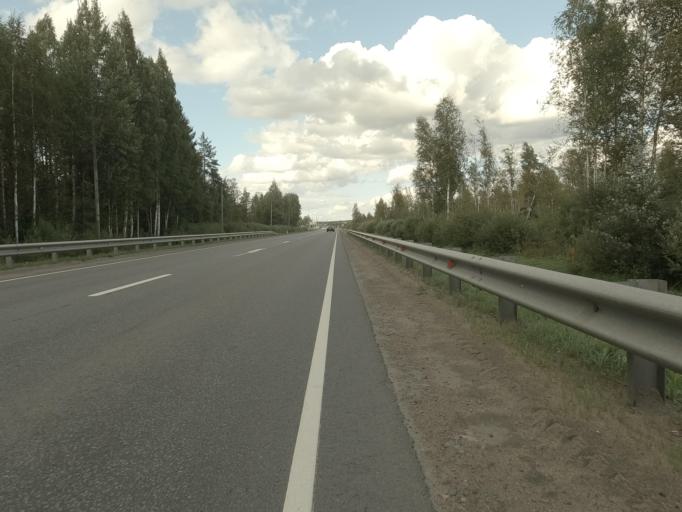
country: RU
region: Leningrad
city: Mga
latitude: 59.7420
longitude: 31.0795
